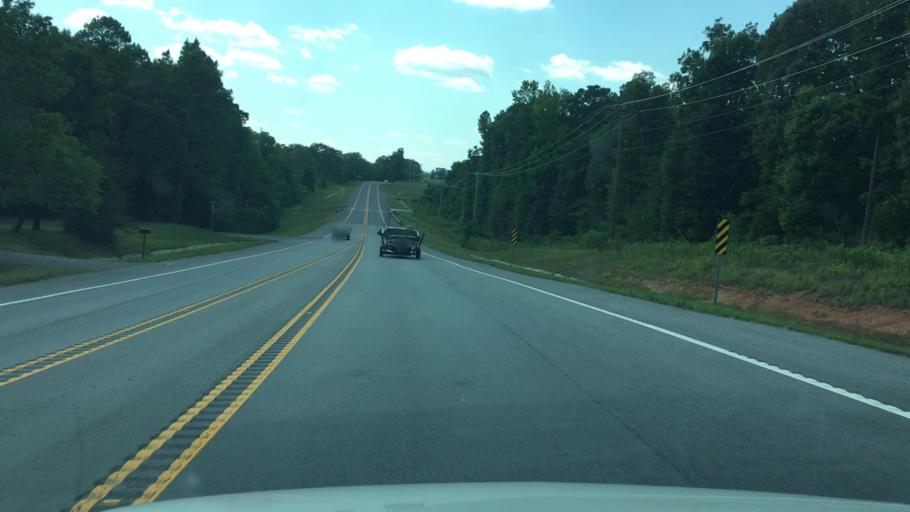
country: US
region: Arkansas
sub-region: Garland County
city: Piney
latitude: 34.5100
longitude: -93.1946
